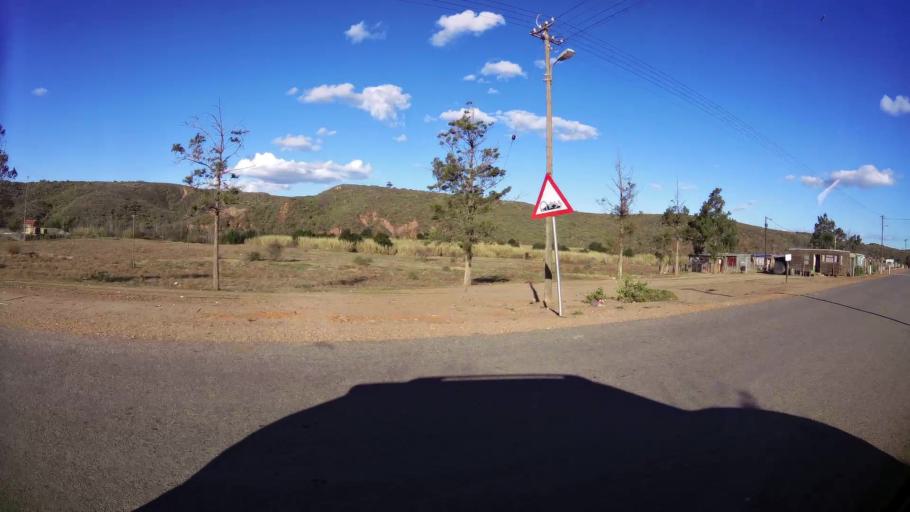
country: ZA
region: Western Cape
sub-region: Eden District Municipality
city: Riversdale
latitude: -34.1046
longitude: 20.9698
